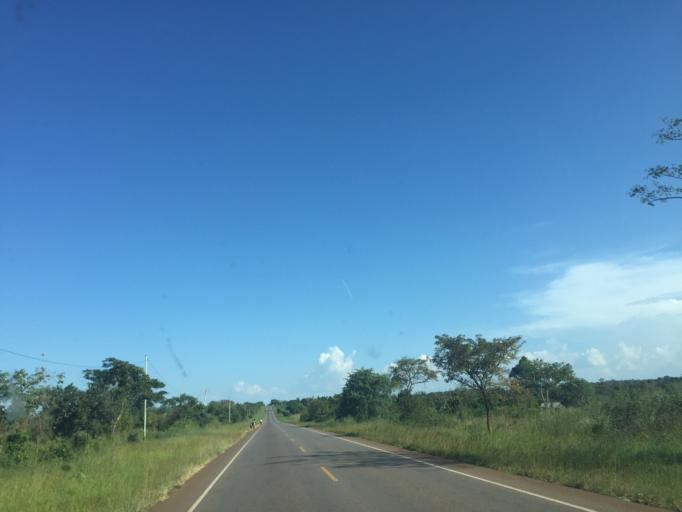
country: UG
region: Central Region
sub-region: Nakasongola District
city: Nakasongola
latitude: 1.3488
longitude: 32.3854
